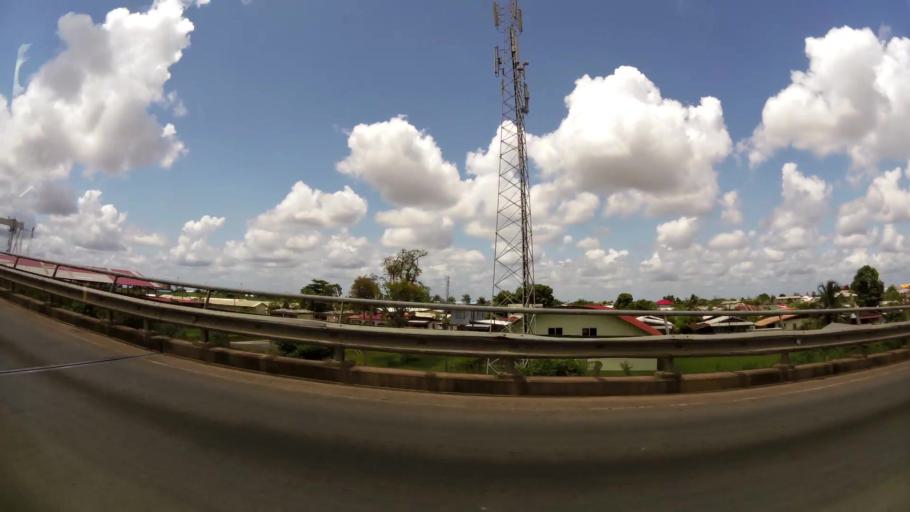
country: SR
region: Paramaribo
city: Paramaribo
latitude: 5.8055
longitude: -55.1705
